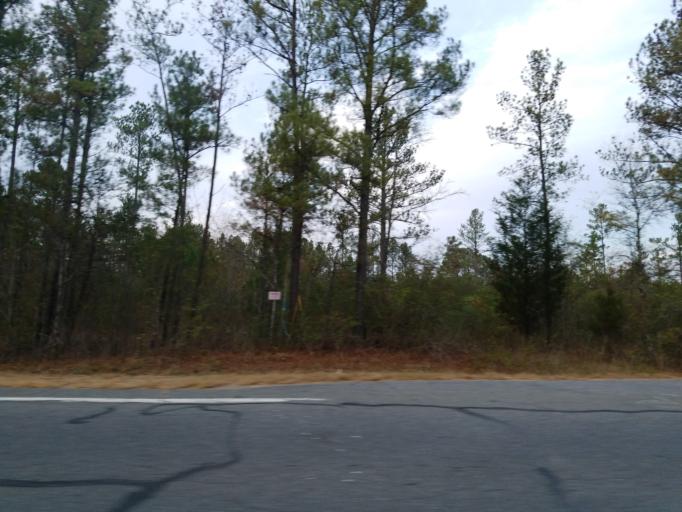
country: US
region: Georgia
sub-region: Murray County
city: Chatsworth
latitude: 34.6066
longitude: -84.8104
